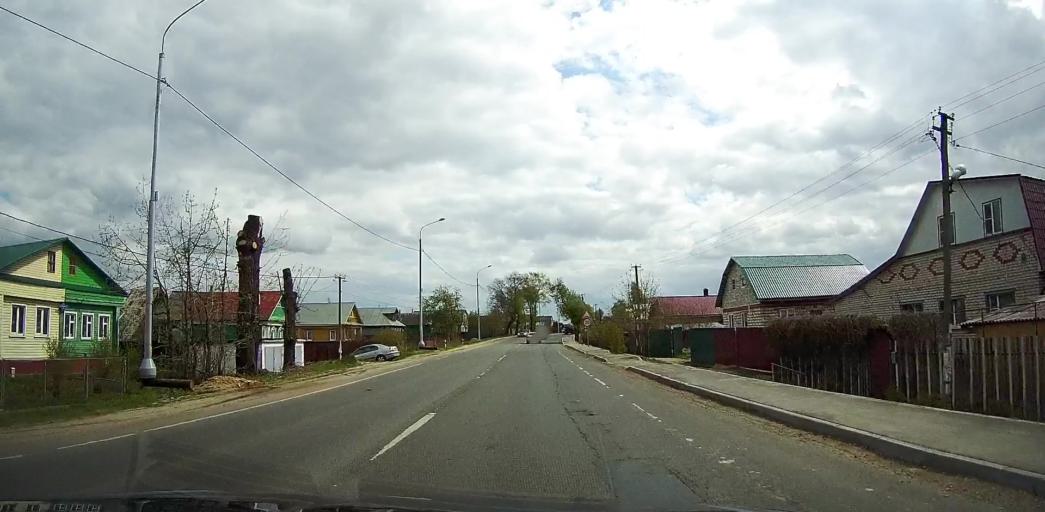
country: RU
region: Moskovskaya
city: Beloozerskiy
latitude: 55.4484
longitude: 38.4499
